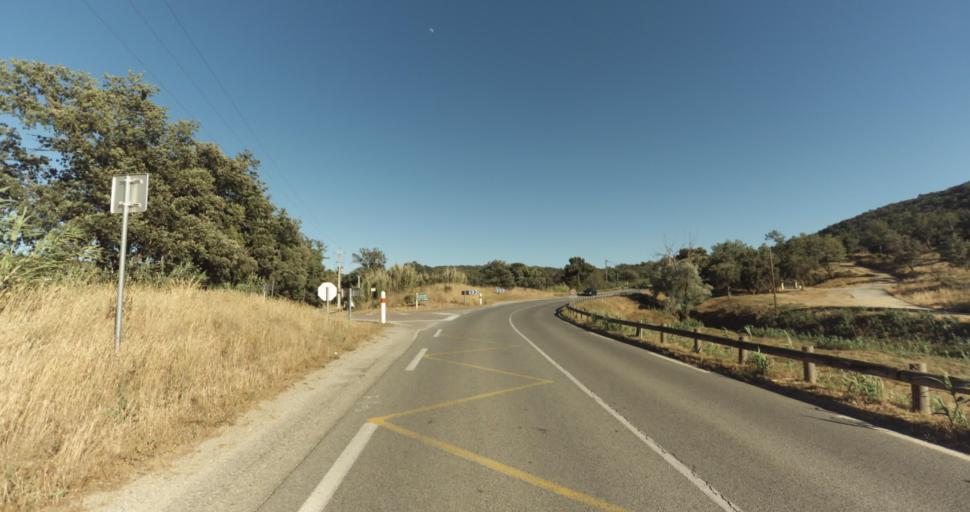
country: FR
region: Provence-Alpes-Cote d'Azur
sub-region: Departement du Var
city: Ramatuelle
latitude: 43.2359
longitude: 6.6100
